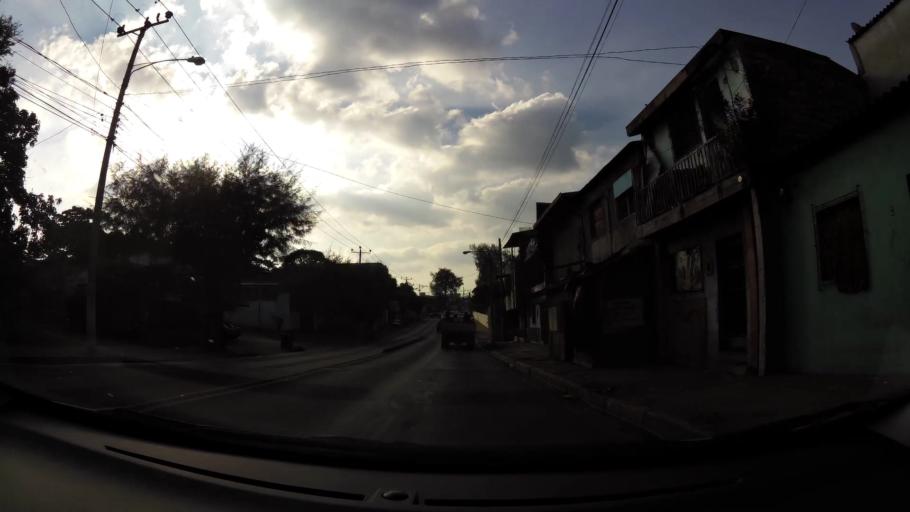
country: SV
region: San Salvador
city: San Salvador
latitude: 13.6923
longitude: -89.1993
